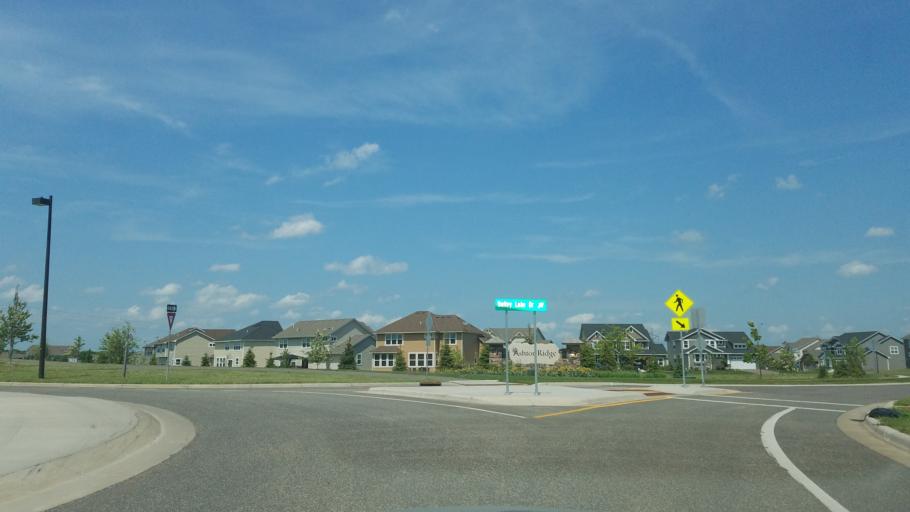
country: US
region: Minnesota
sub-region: Washington County
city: Woodbury
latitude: 44.8810
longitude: -92.9236
